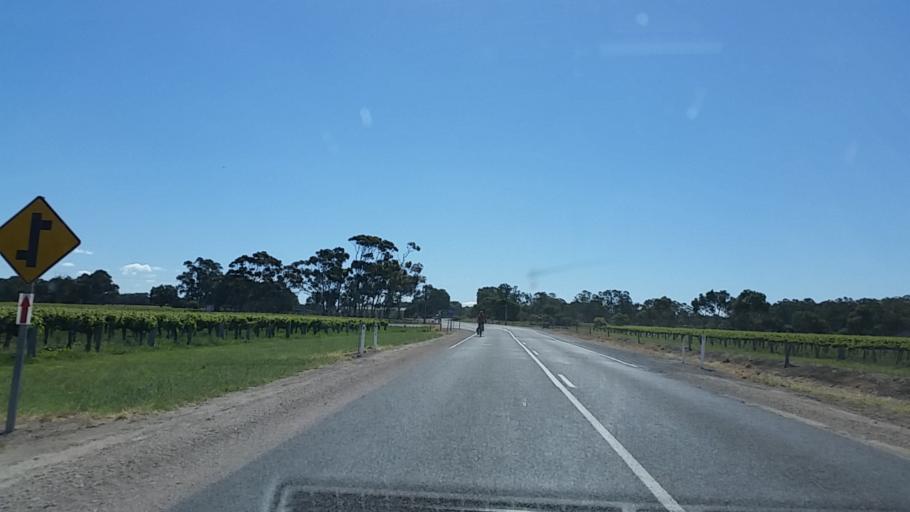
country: AU
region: South Australia
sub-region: Alexandrina
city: Langhorne Creek
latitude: -35.3095
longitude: 139.0550
